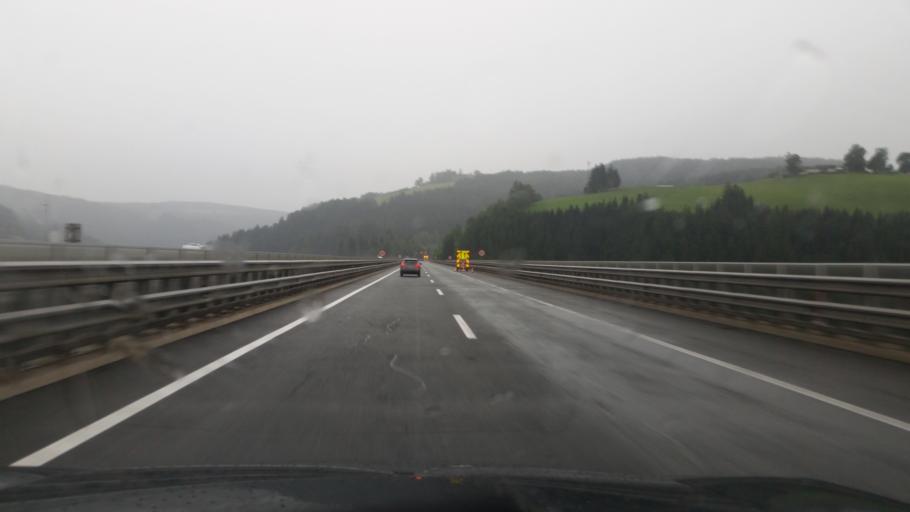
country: AT
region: Carinthia
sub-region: Politischer Bezirk Wolfsberg
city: Bad Sankt Leonhard im Lavanttal
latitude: 46.9221
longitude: 14.8401
